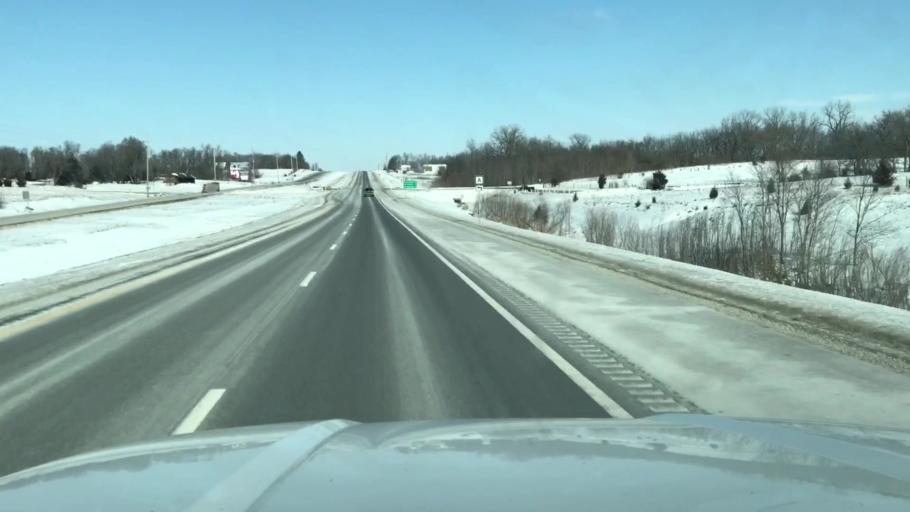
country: US
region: Missouri
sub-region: Nodaway County
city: Maryville
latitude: 40.1978
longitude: -94.8677
